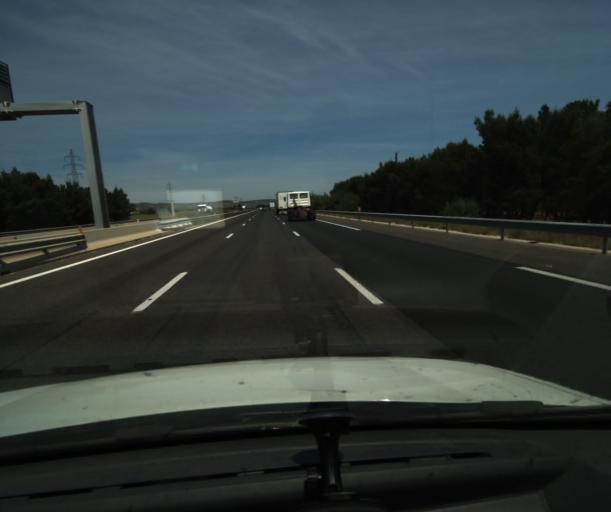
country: FR
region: Languedoc-Roussillon
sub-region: Departement des Pyrenees-Orientales
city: Salses-le-Chateau
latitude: 42.8040
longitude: 2.9002
